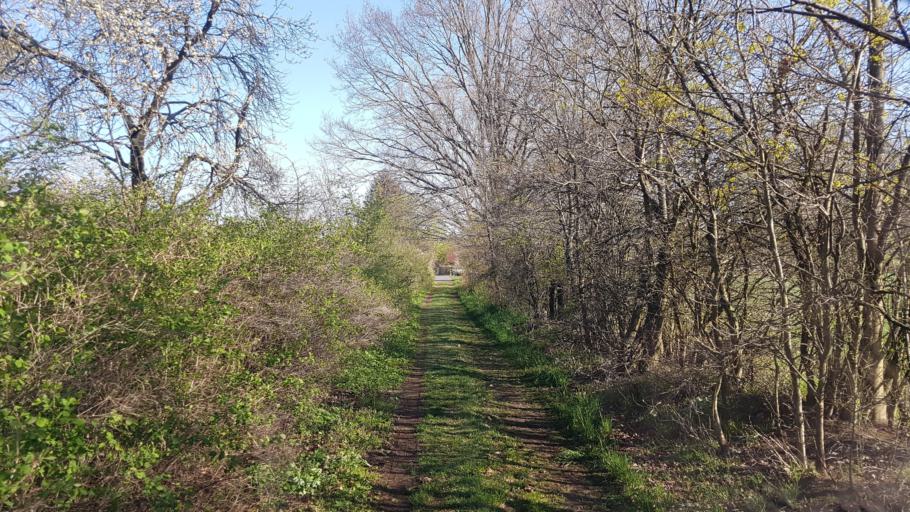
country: DE
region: Brandenburg
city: Bronkow
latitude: 51.6658
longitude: 13.9164
